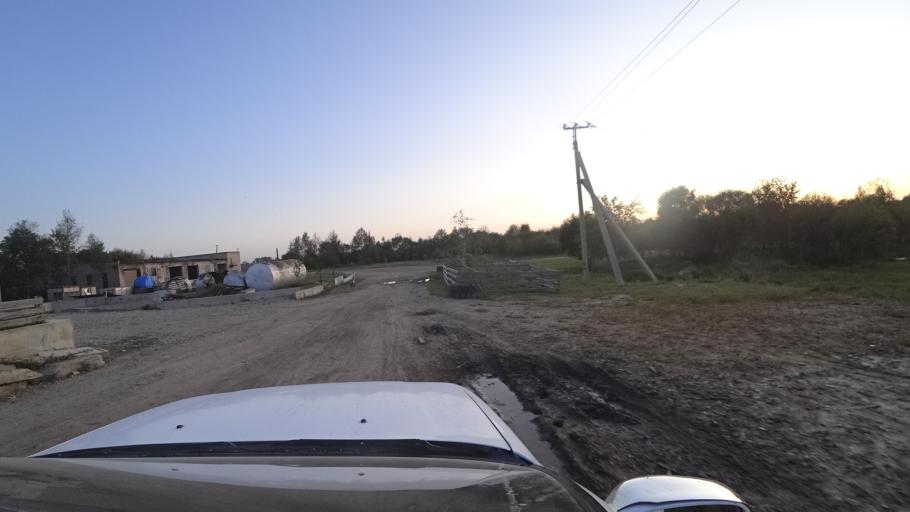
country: RU
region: Primorskiy
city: Dal'nerechensk
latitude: 45.9447
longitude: 133.7611
